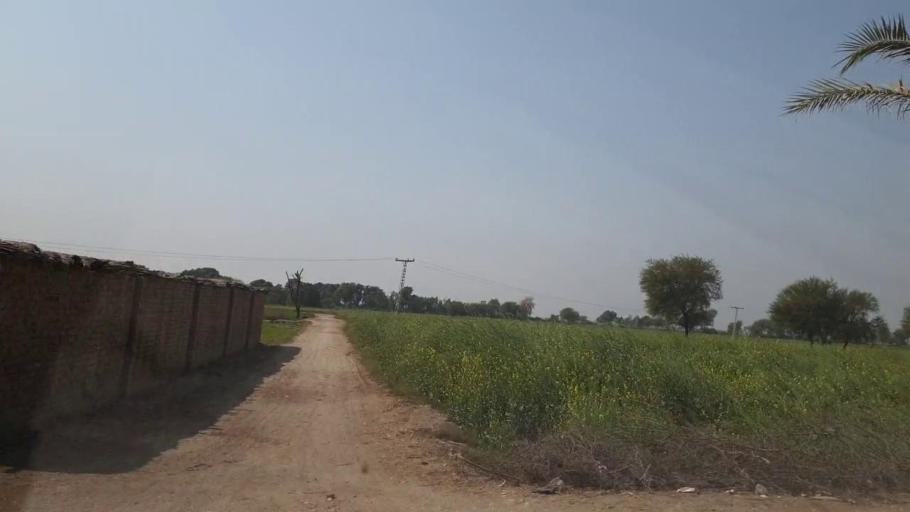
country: PK
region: Sindh
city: Mirpur Khas
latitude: 25.6340
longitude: 69.1386
